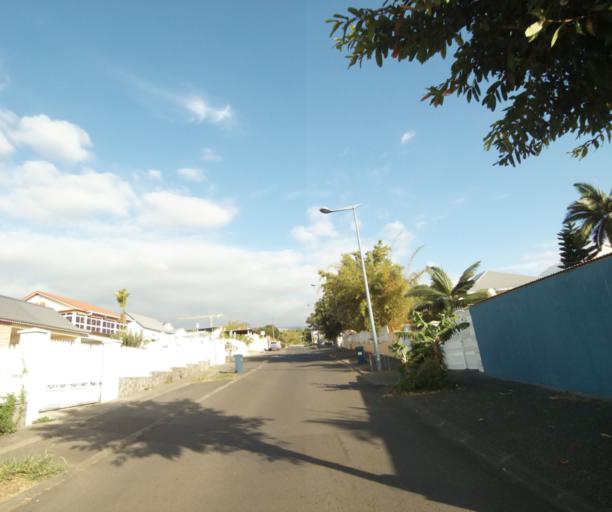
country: RE
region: Reunion
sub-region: Reunion
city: Saint-Paul
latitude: -21.0472
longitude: 55.2581
